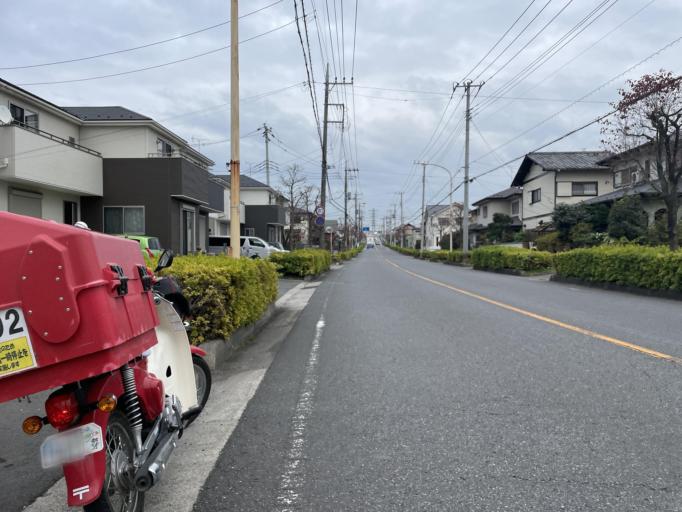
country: JP
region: Saitama
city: Shiraoka
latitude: 35.9968
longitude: 139.6579
